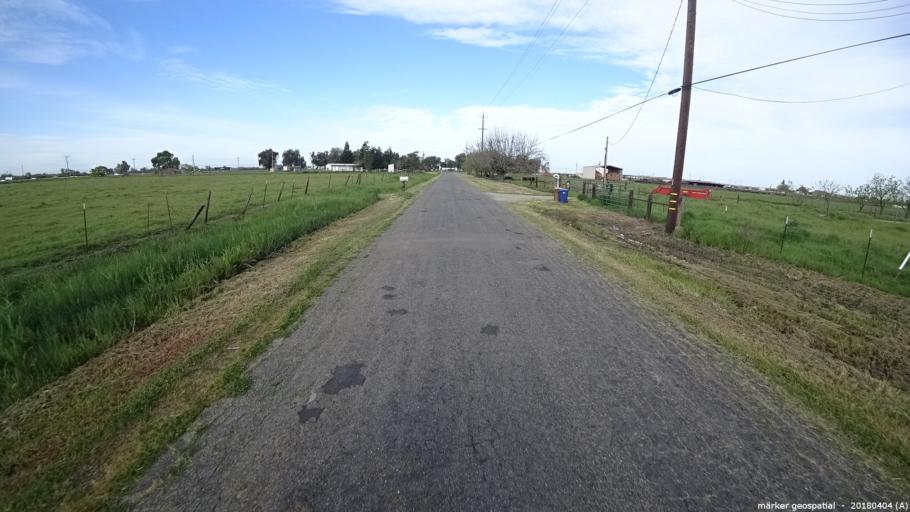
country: US
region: California
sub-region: Sacramento County
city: Galt
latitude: 38.3025
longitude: -121.3140
